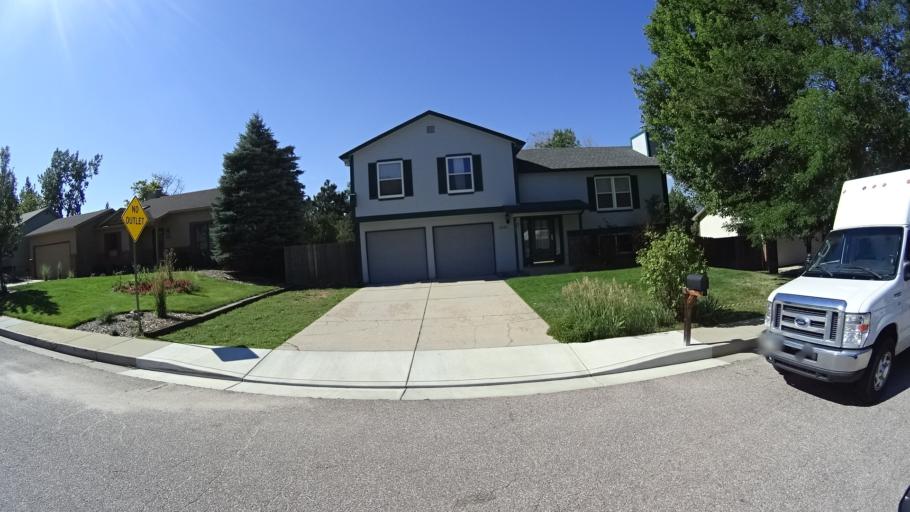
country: US
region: Colorado
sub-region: El Paso County
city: Air Force Academy
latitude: 38.9408
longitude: -104.7869
